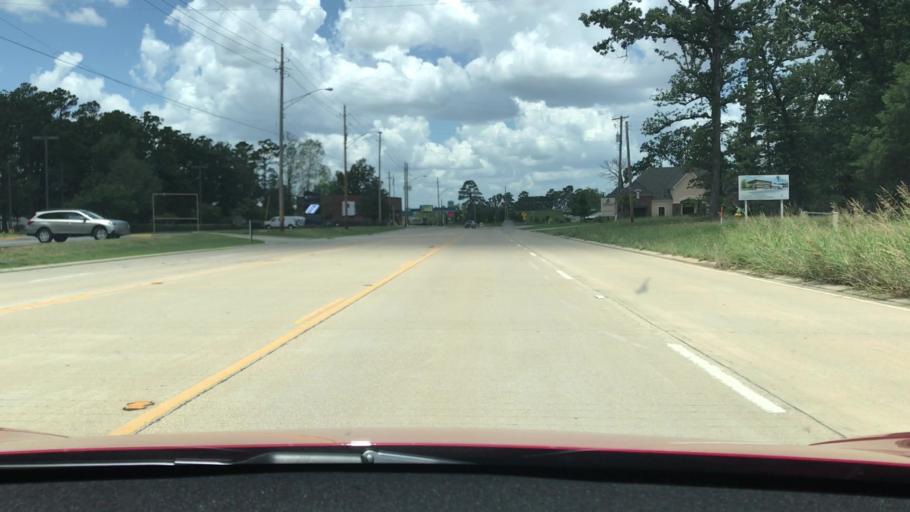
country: US
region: Louisiana
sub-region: Bossier Parish
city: Bossier City
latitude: 32.3980
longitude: -93.7315
